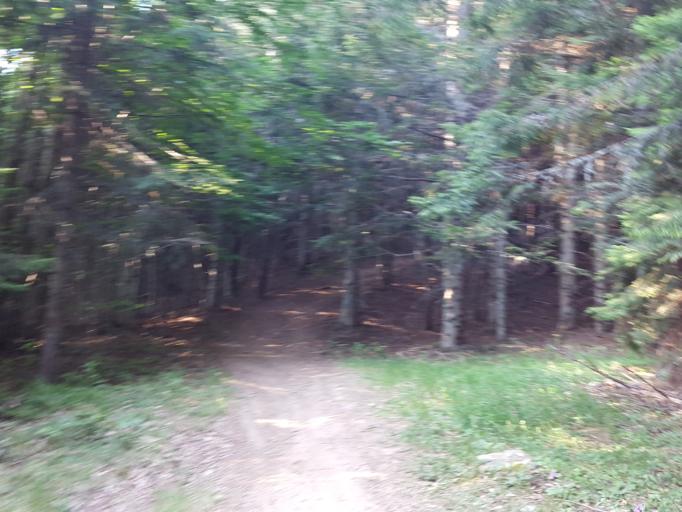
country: IT
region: Tuscany
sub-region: Provincia di Pistoia
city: Abetone
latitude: 44.1558
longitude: 10.6767
